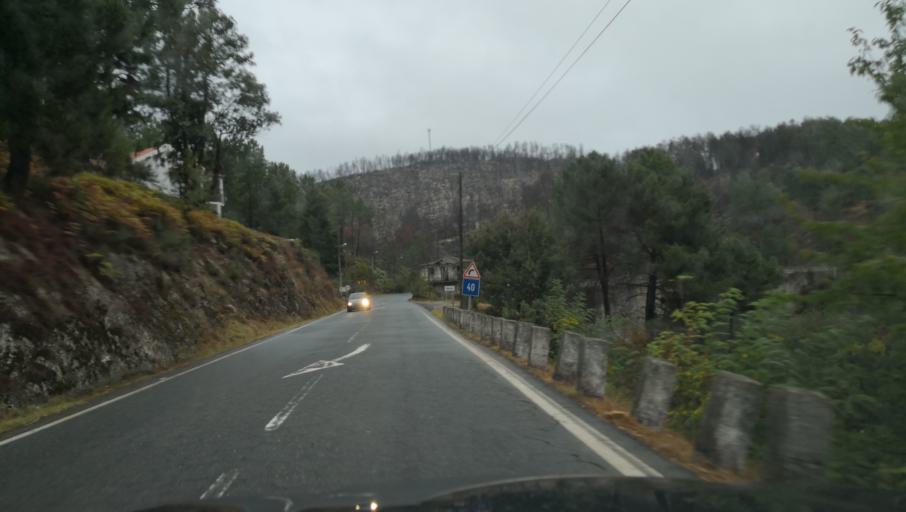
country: PT
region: Vila Real
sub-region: Sabrosa
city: Sabrosa
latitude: 41.3509
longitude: -7.5926
